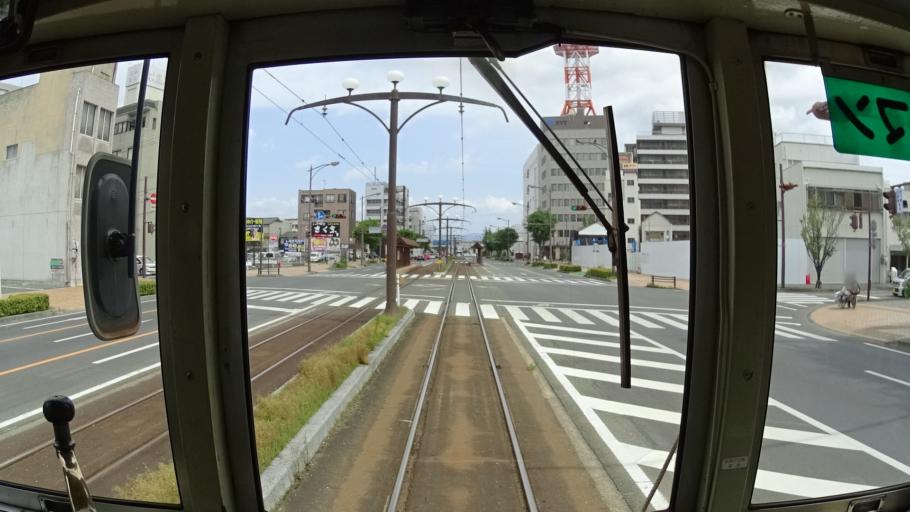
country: JP
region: Aichi
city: Toyohashi
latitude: 34.7654
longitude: 137.3903
